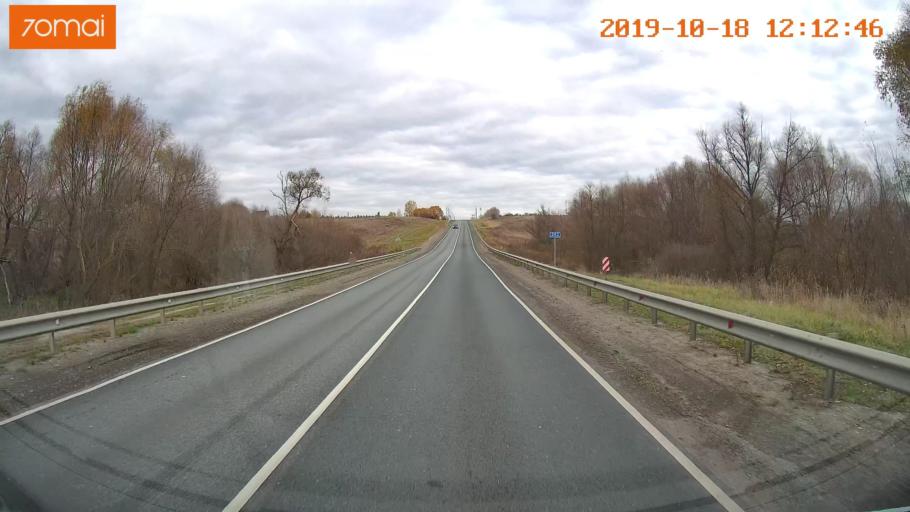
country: RU
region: Rjazan
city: Zakharovo
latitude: 54.4150
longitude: 39.3619
